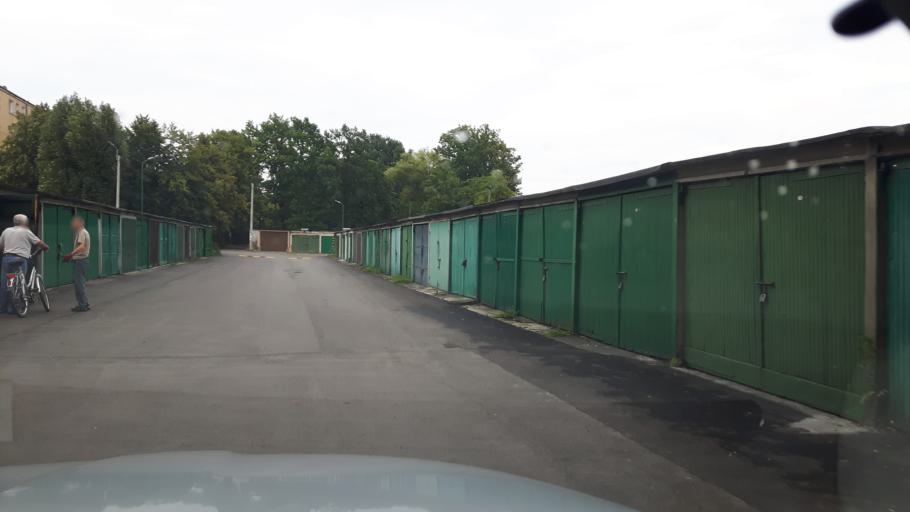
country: PL
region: Masovian Voivodeship
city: Zielonka
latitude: 52.3144
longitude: 21.1622
